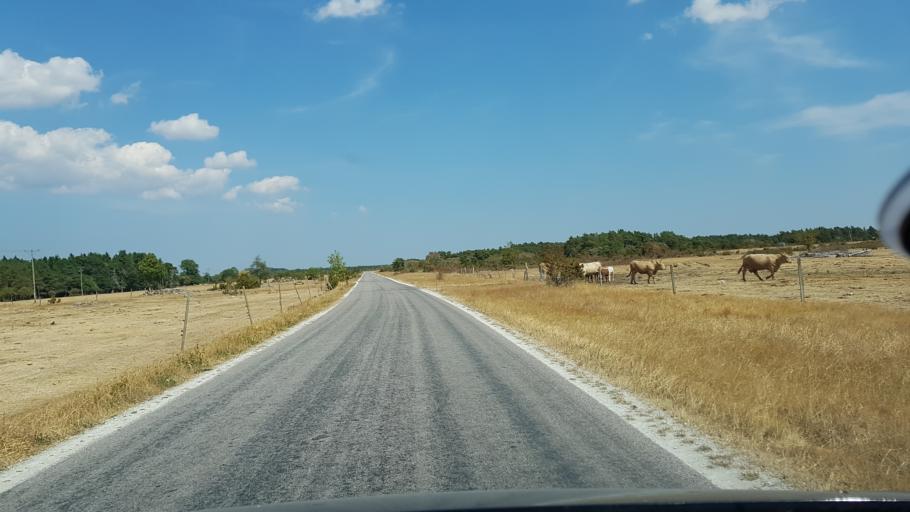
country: SE
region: Gotland
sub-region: Gotland
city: Visby
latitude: 57.6583
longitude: 18.3676
